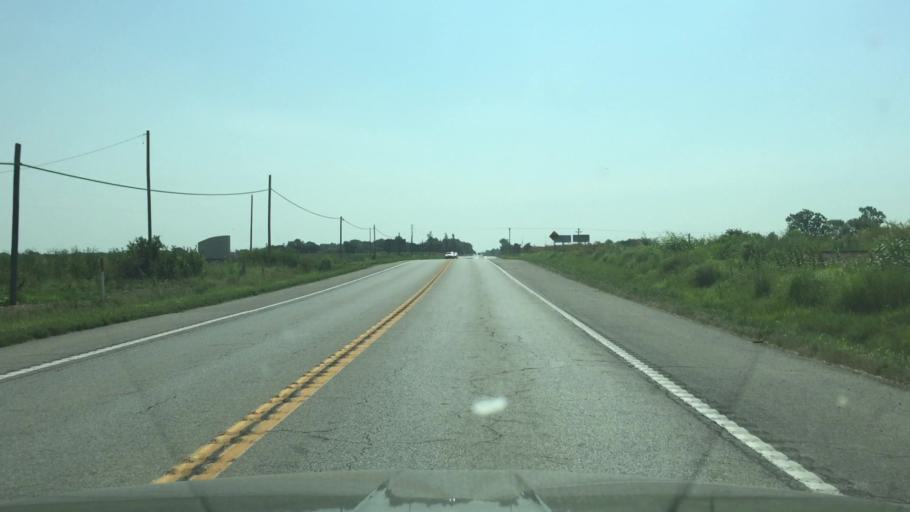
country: US
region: Missouri
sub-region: Pettis County
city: Sedalia
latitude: 38.6964
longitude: -93.1756
